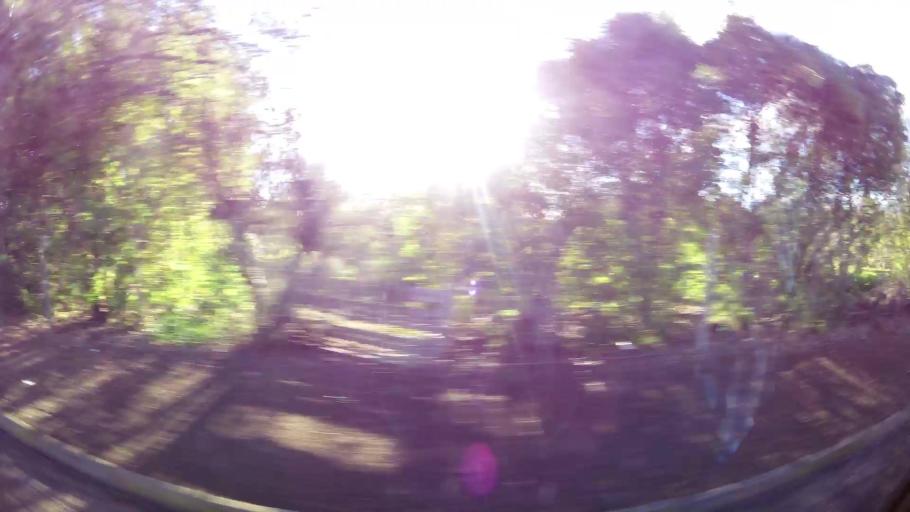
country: ZA
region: Western Cape
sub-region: Eden District Municipality
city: Riversdale
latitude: -34.0970
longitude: 20.9569
